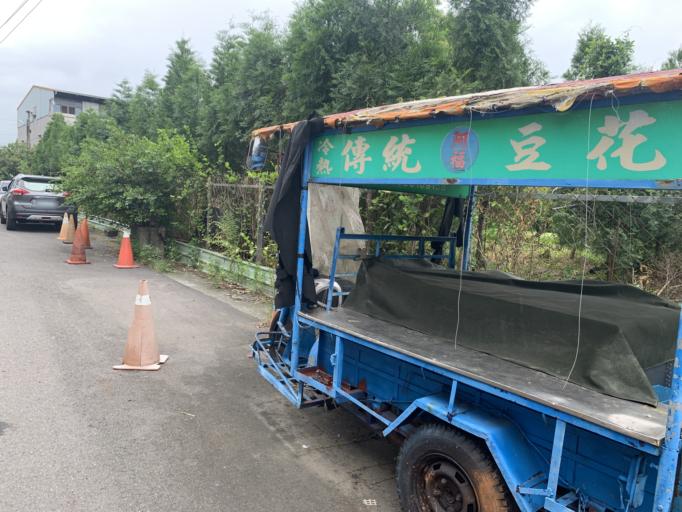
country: TW
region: Taiwan
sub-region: Chiayi
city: Jiayi Shi
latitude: 23.4908
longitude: 120.4779
